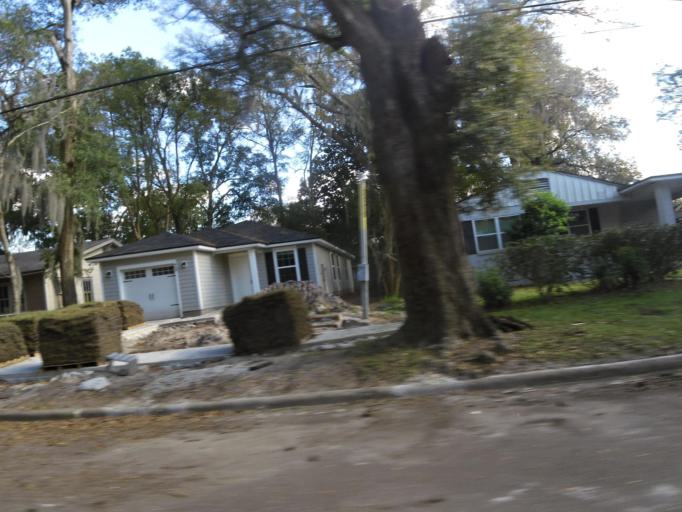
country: US
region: Florida
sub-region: Duval County
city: Jacksonville
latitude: 30.3819
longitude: -81.6603
